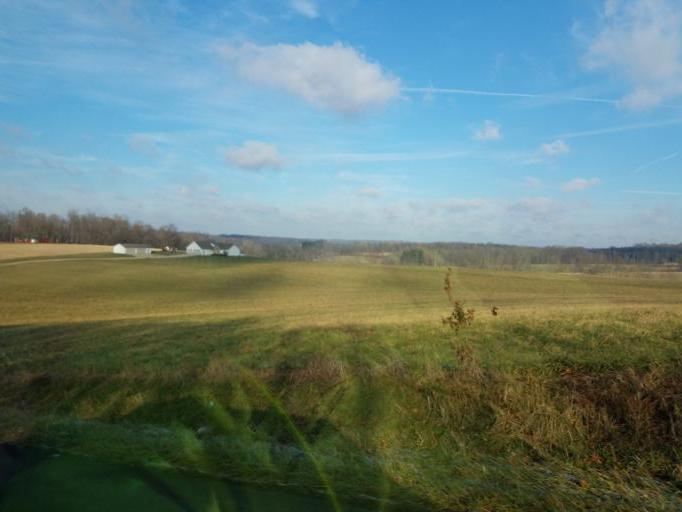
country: US
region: Ohio
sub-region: Knox County
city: Gambier
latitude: 40.4937
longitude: -82.4064
